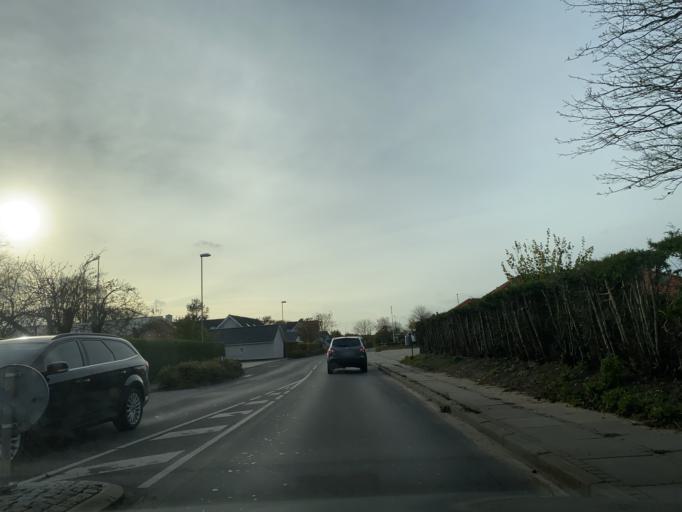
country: DK
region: Central Jutland
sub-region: Skanderborg Kommune
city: Skovby
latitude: 56.1583
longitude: 9.9461
